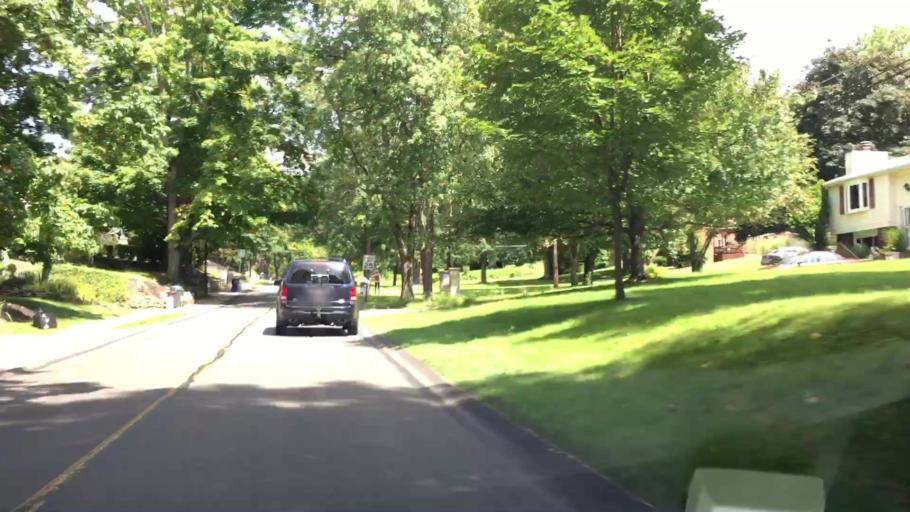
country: US
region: Pennsylvania
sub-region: Allegheny County
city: Bethel Park
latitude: 40.3092
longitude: -80.0302
